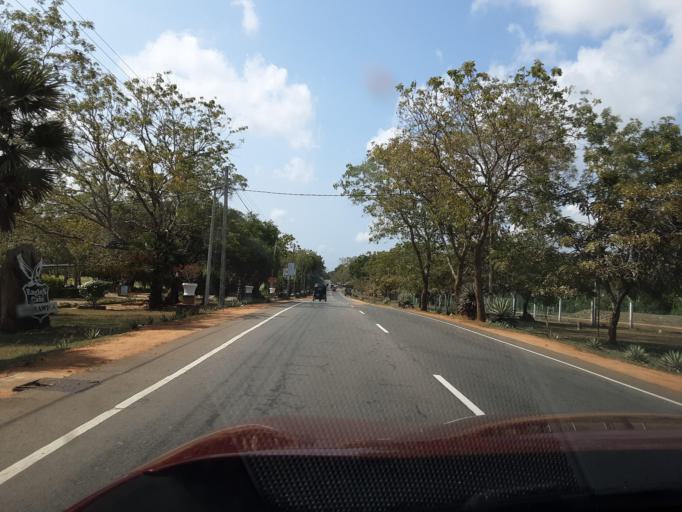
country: LK
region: Southern
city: Tangalla
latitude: 6.2509
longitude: 81.2277
